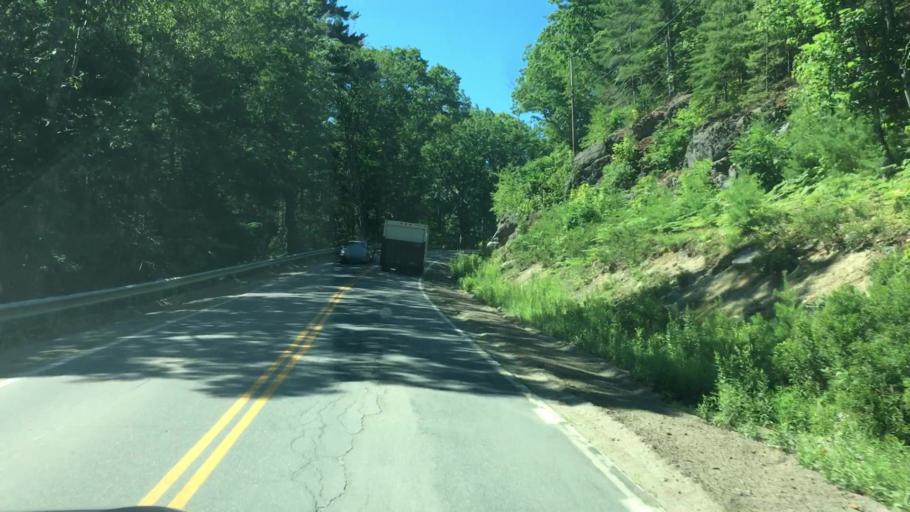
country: US
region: Maine
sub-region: Hancock County
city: Sedgwick
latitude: 44.3615
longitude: -68.5750
